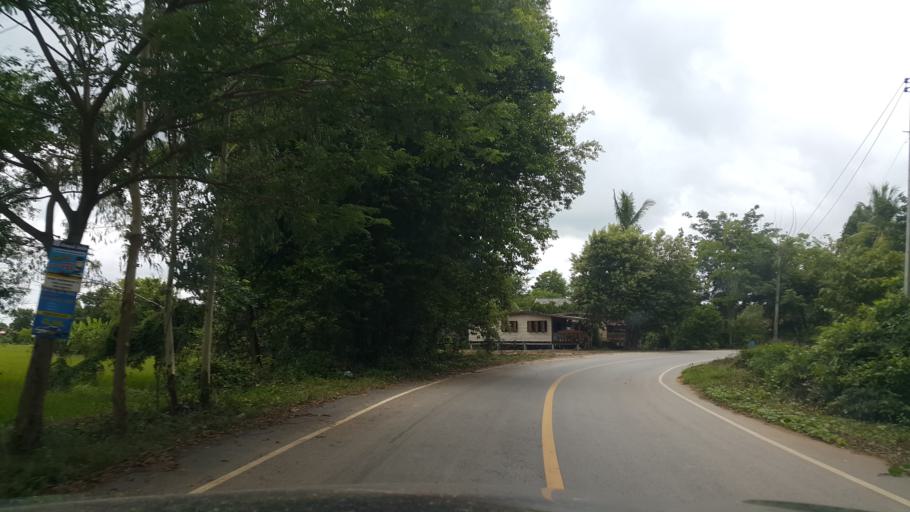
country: TH
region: Sukhothai
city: Kong Krailat
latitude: 16.9088
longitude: 99.8854
